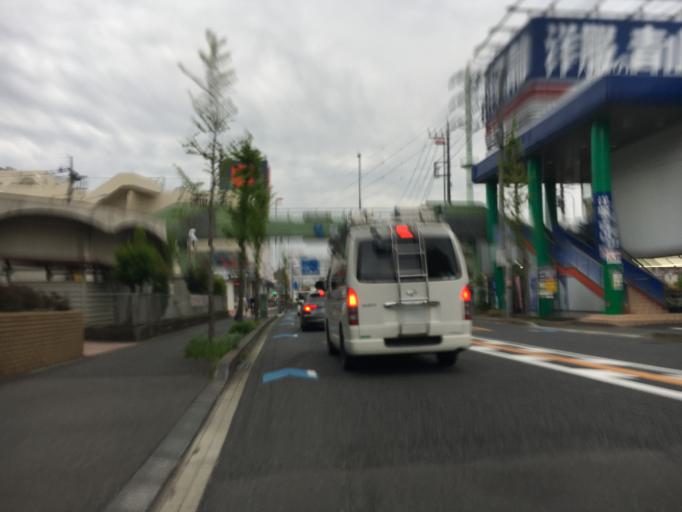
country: JP
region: Saitama
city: Yono
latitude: 35.8854
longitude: 139.6312
